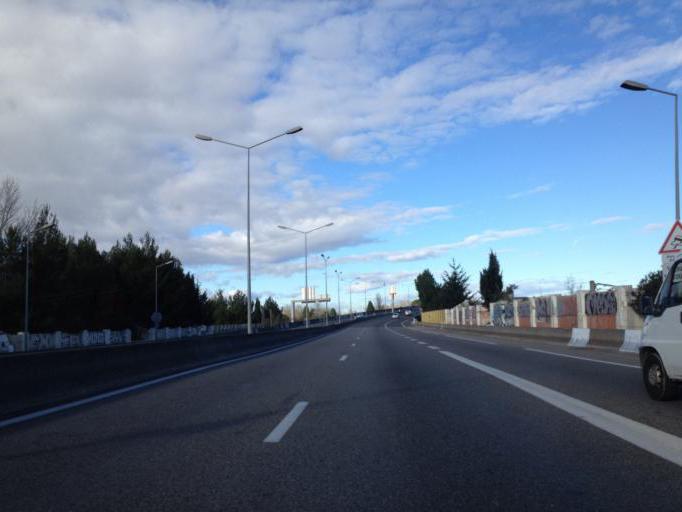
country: FR
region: Provence-Alpes-Cote d'Azur
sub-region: Departement du Vaucluse
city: Le Pontet
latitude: 43.9540
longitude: 4.8401
